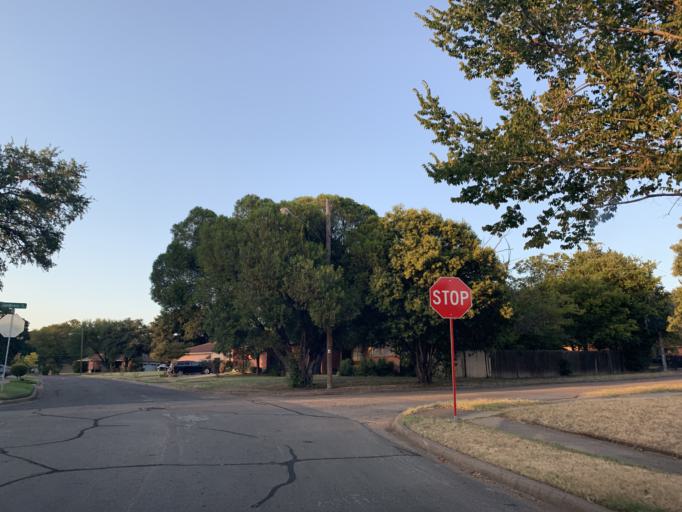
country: US
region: Texas
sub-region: Dallas County
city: Dallas
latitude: 32.6958
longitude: -96.8087
